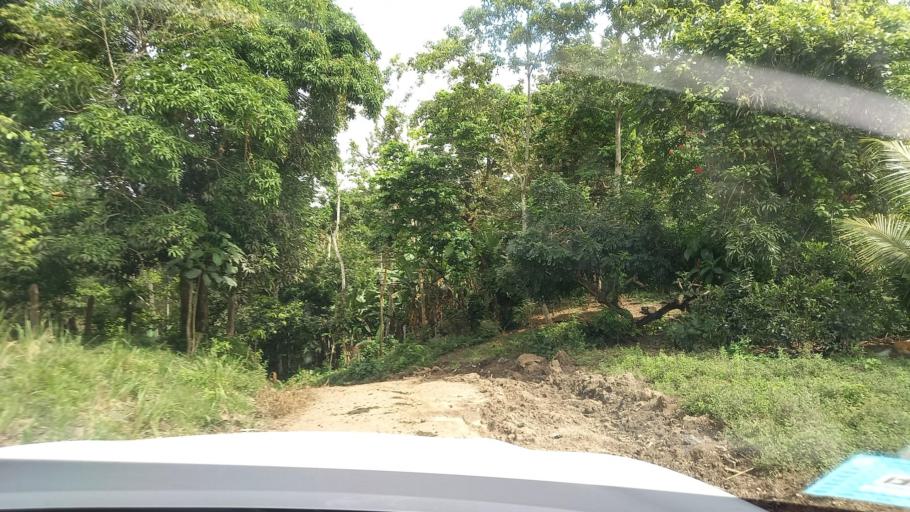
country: NI
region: Jinotega
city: San Jose de Bocay
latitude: 13.4147
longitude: -85.7037
